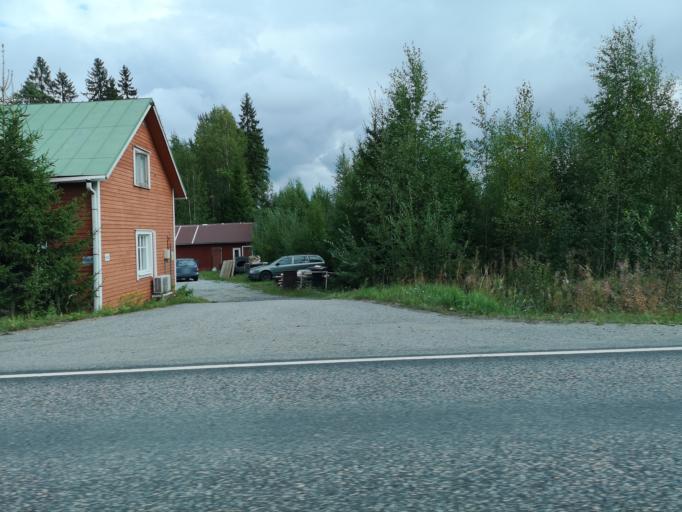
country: FI
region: Central Finland
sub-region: Jyvaeskylae
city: Hankasalmi
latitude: 62.3633
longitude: 26.4504
